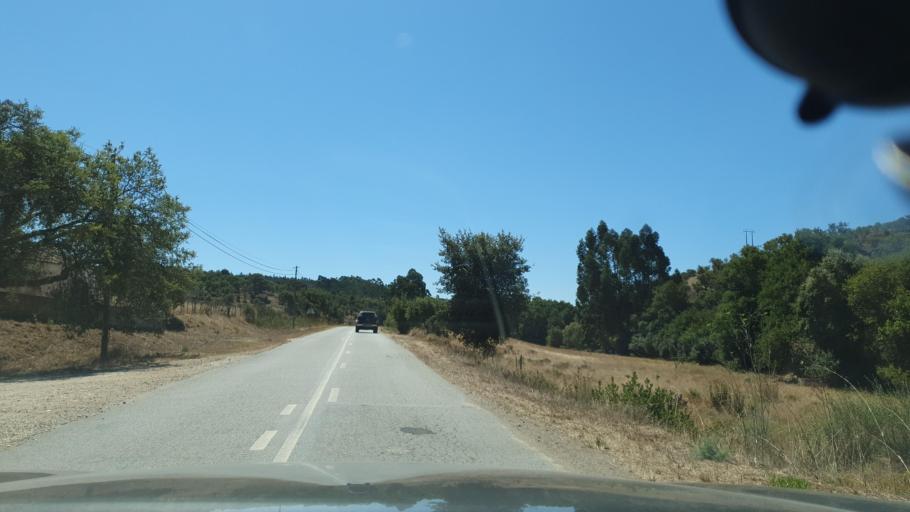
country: PT
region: Faro
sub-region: Monchique
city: Monchique
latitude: 37.4334
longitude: -8.5597
